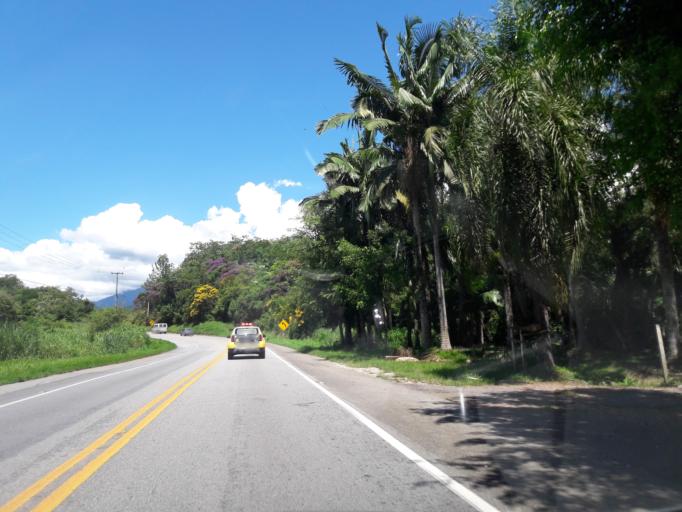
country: BR
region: Parana
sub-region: Antonina
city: Antonina
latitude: -25.5153
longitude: -48.8059
